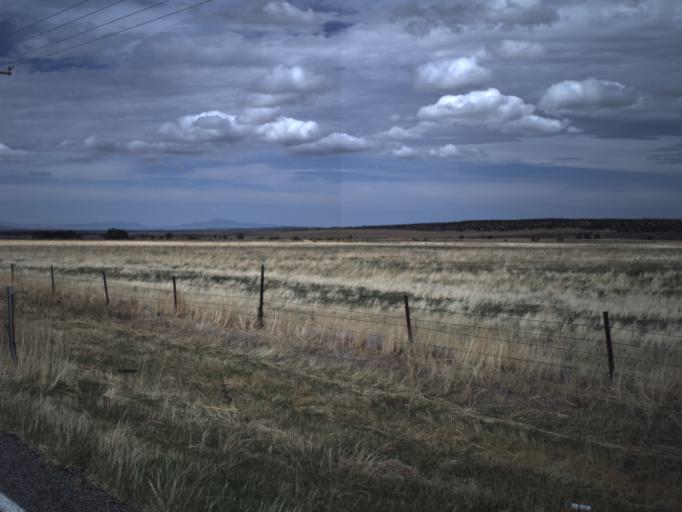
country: US
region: Utah
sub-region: Millard County
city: Fillmore
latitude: 38.9791
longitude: -112.3752
